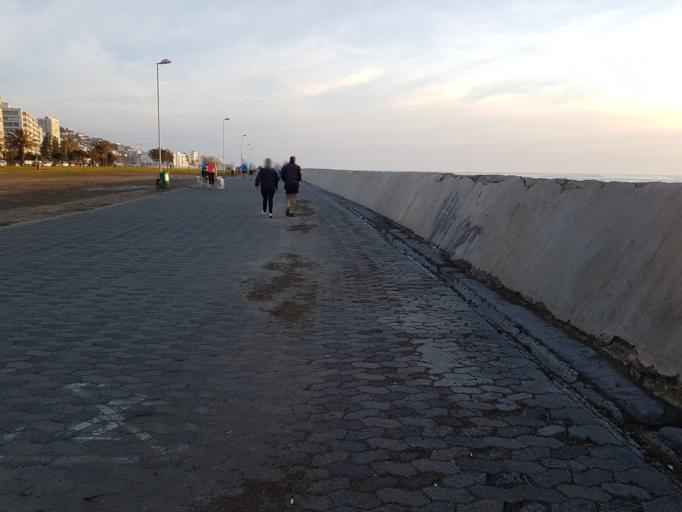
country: ZA
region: Western Cape
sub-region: City of Cape Town
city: Cape Town
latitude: -33.9098
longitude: 18.3899
